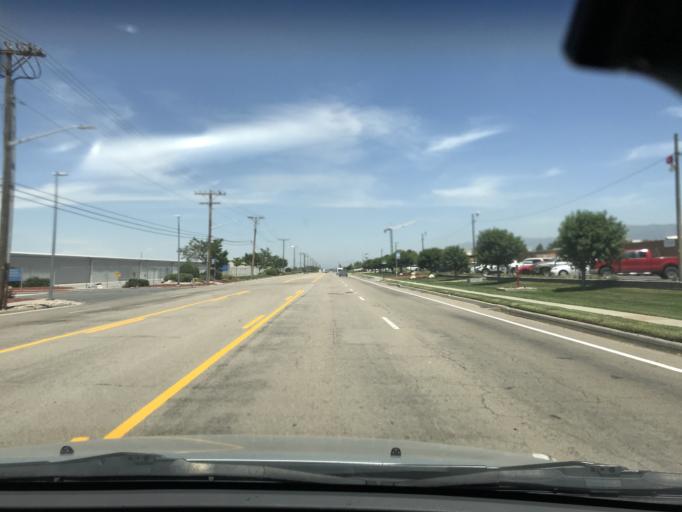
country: US
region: Utah
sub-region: Salt Lake County
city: Salt Lake City
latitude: 40.7760
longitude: -111.9535
